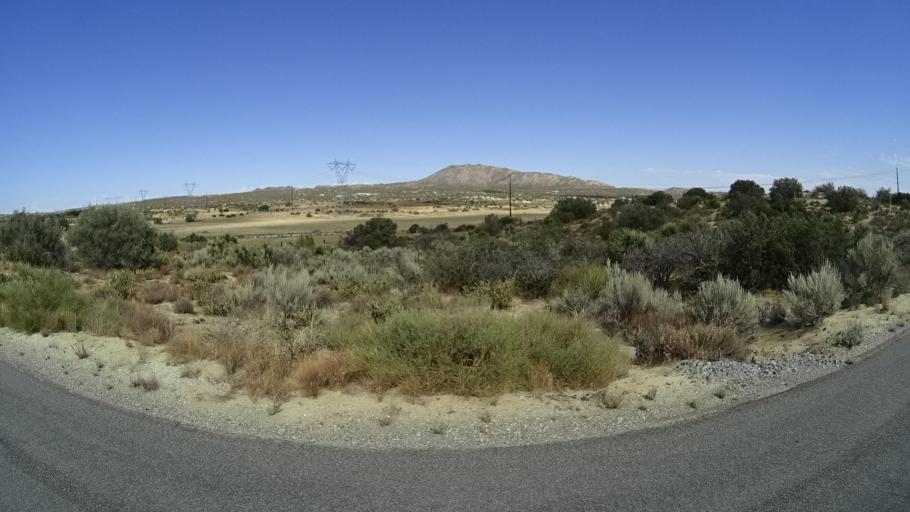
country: MX
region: Baja California
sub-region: Tecate
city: Cereso del Hongo
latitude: 32.6826
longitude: -116.2621
